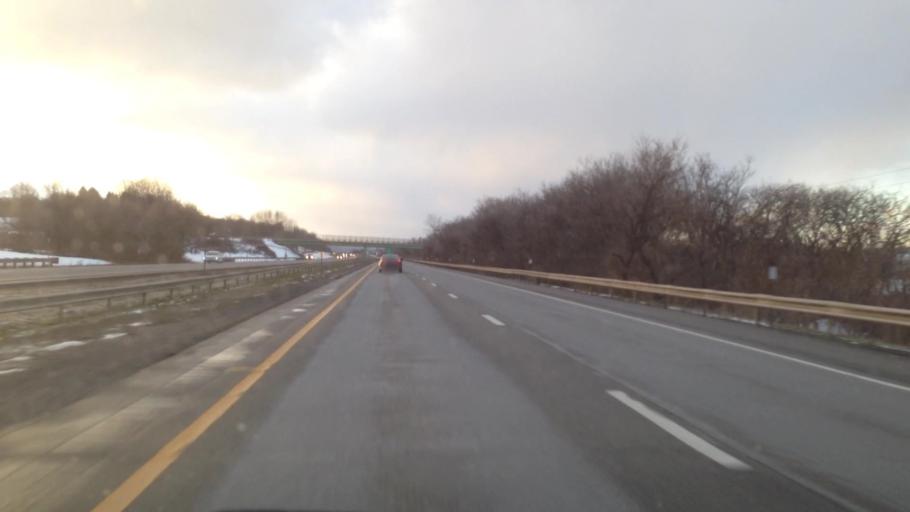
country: US
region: New York
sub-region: Herkimer County
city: Herkimer
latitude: 43.0144
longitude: -74.9428
